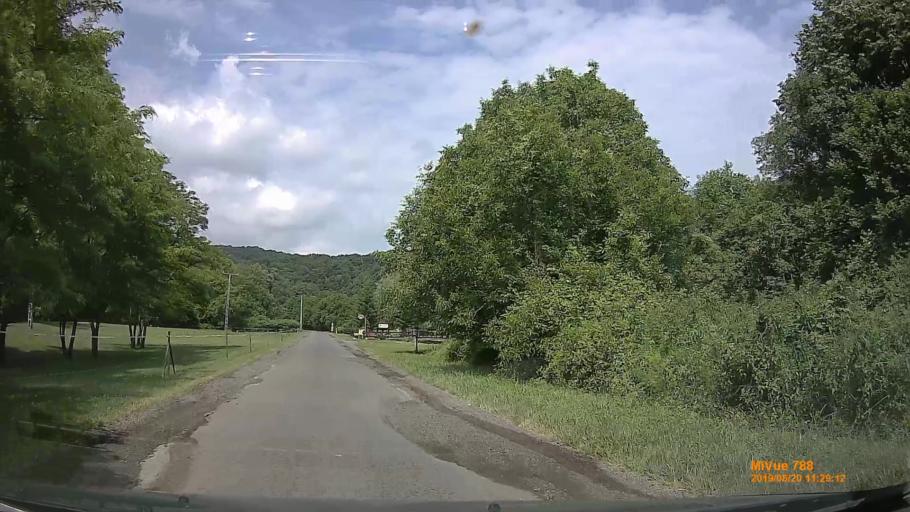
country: HU
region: Baranya
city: Mecseknadasd
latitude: 46.2251
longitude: 18.4434
